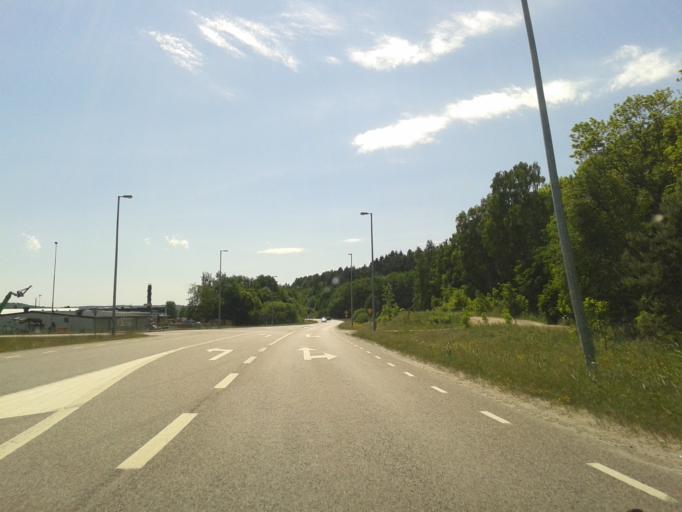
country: SE
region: Vaestra Goetaland
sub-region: Kungalvs Kommun
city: Kungalv
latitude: 57.8877
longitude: 11.9871
